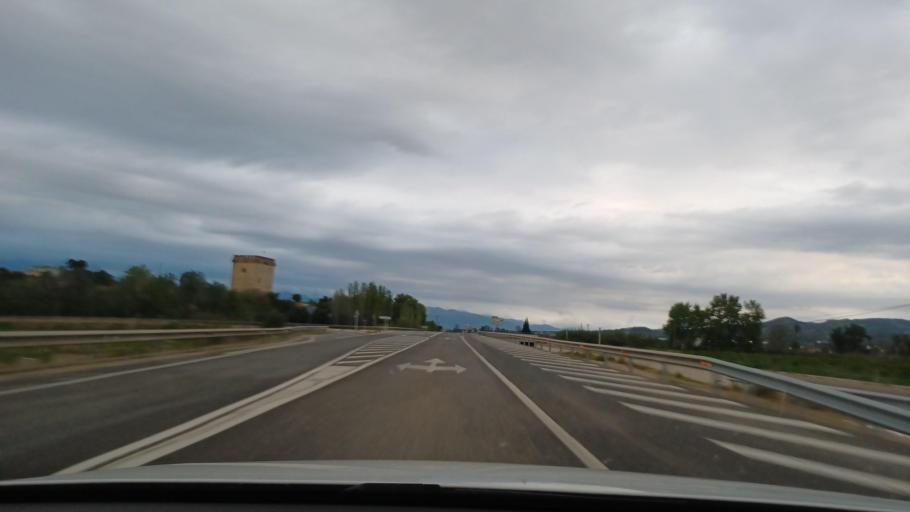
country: ES
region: Catalonia
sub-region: Provincia de Tarragona
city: Amposta
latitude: 40.7410
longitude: 0.5644
